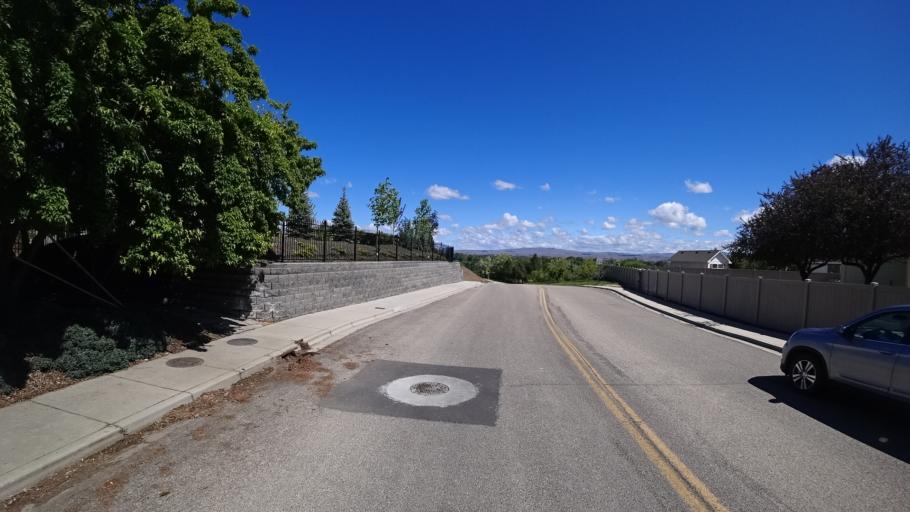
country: US
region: Idaho
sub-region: Ada County
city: Eagle
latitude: 43.6697
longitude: -116.3746
